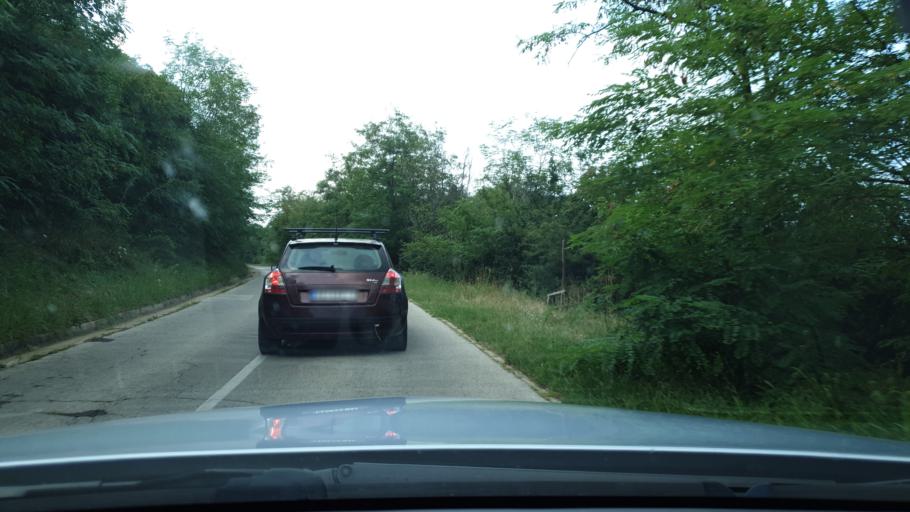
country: RS
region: Autonomna Pokrajina Vojvodina
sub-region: Juznobanatski Okrug
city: Vrsac
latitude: 45.1209
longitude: 21.3299
